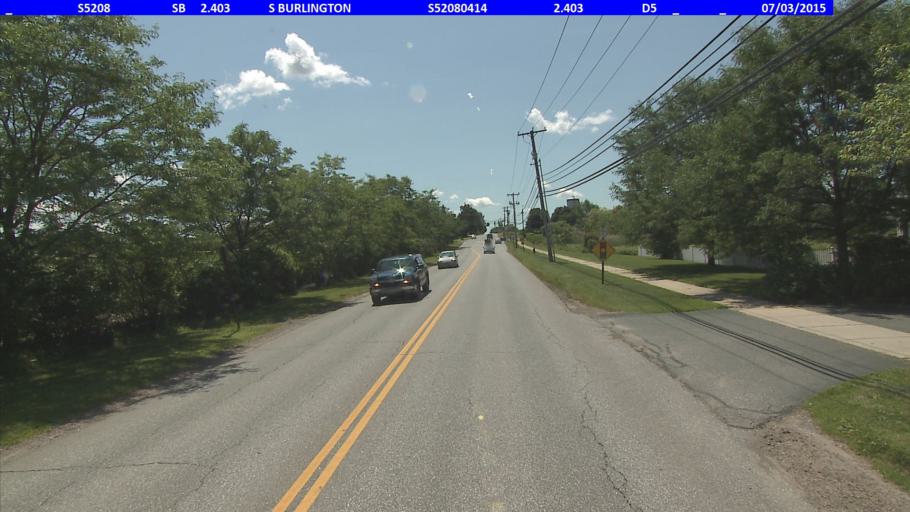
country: US
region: Vermont
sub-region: Chittenden County
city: South Burlington
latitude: 44.4451
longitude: -73.1774
